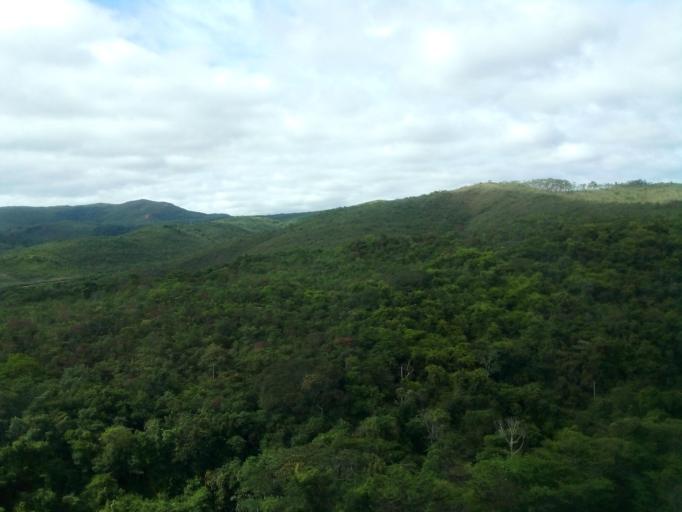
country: BR
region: Minas Gerais
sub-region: Caete
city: Caete
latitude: -19.8954
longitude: -43.7385
